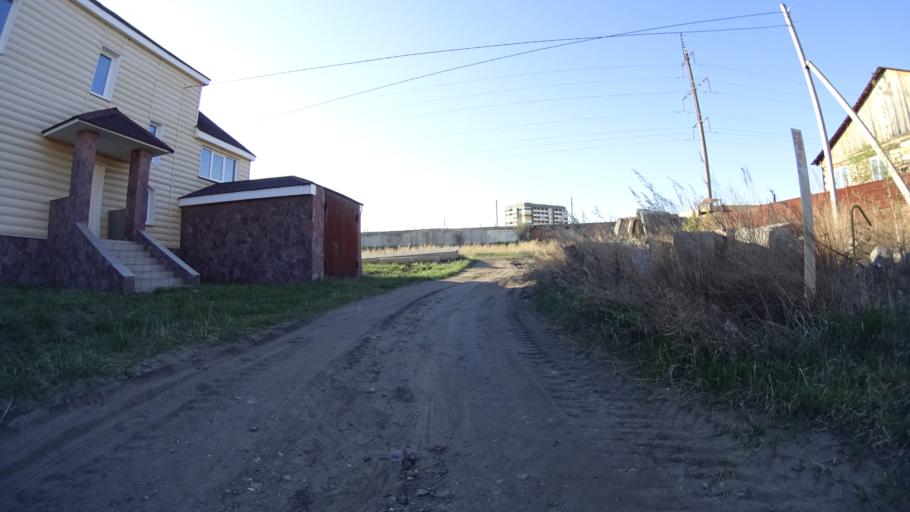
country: RU
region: Chelyabinsk
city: Troitsk
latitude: 54.0700
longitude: 61.5315
